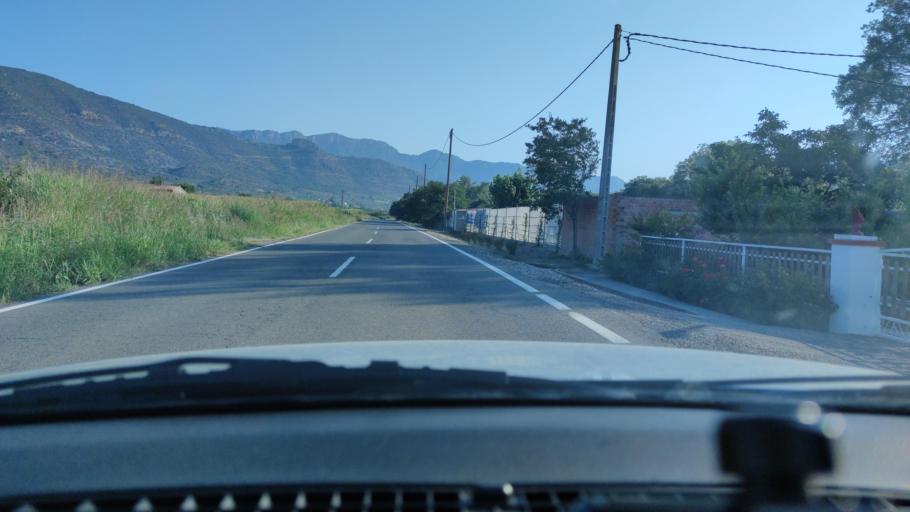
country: ES
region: Catalonia
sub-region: Provincia de Lleida
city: Balaguer
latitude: 41.8452
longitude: 0.8245
